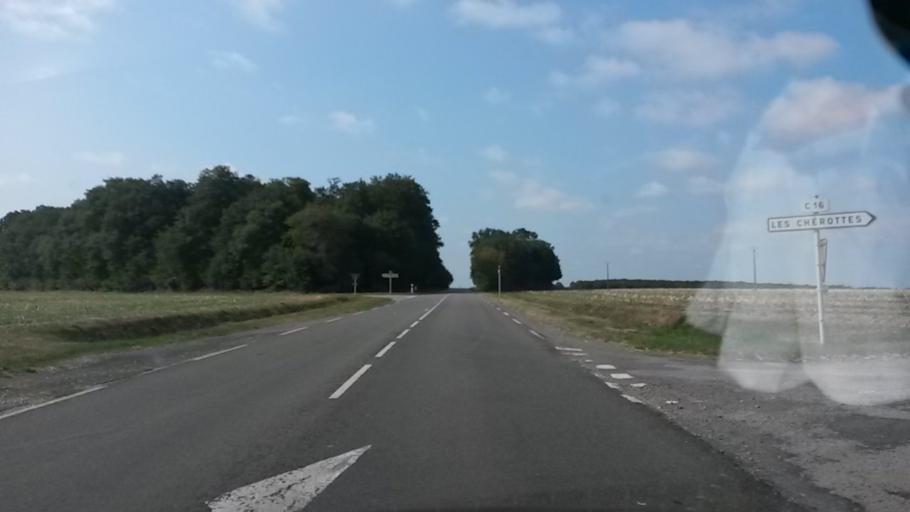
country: FR
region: Haute-Normandie
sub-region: Departement de l'Eure
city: Damville
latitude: 48.8566
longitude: 1.0630
